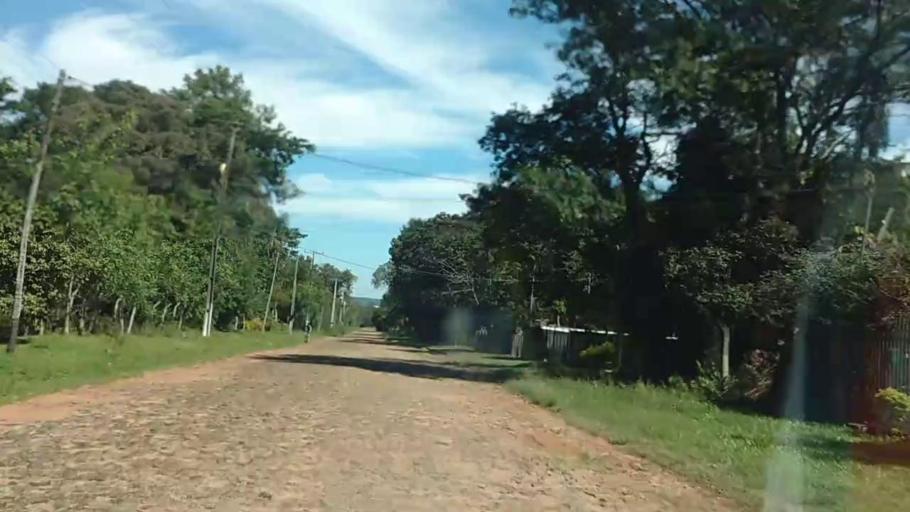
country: PY
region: Cordillera
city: San Bernardino
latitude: -25.3296
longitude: -57.2683
